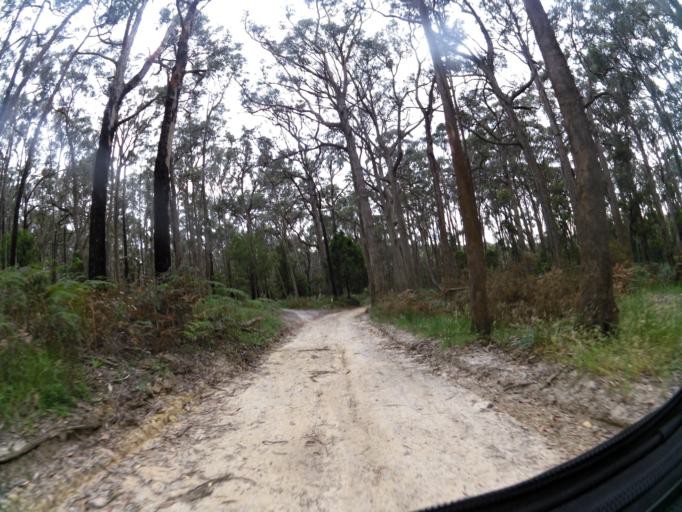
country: AU
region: Victoria
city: Brown Hill
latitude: -37.5192
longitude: 143.9117
